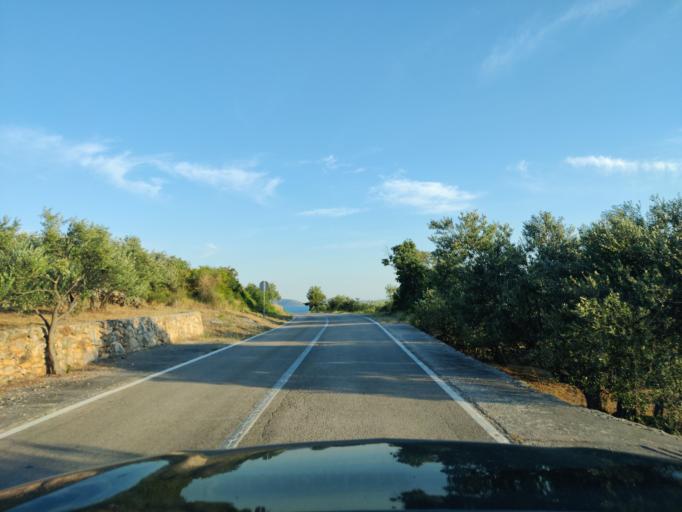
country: HR
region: Sibensko-Kniniska
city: Tribunj
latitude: 43.7847
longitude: 15.7271
